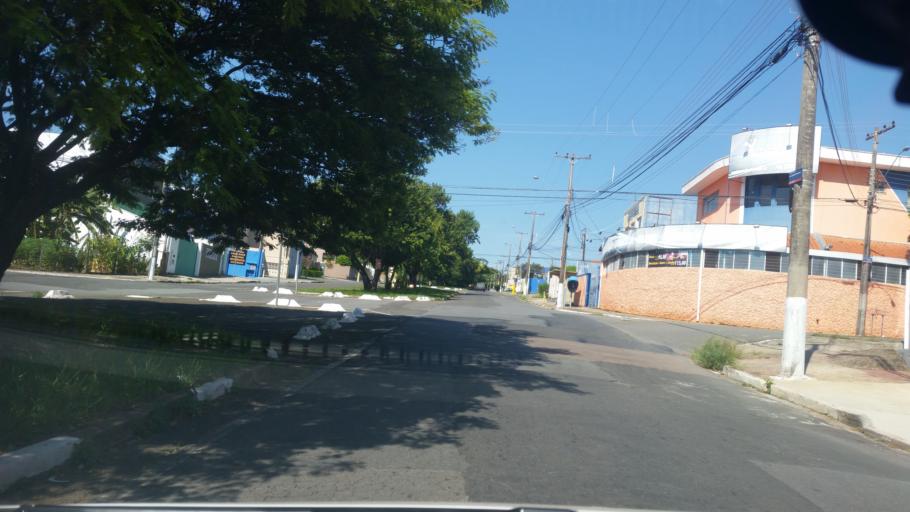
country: BR
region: Sao Paulo
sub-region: Campinas
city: Campinas
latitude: -22.8510
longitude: -47.0664
